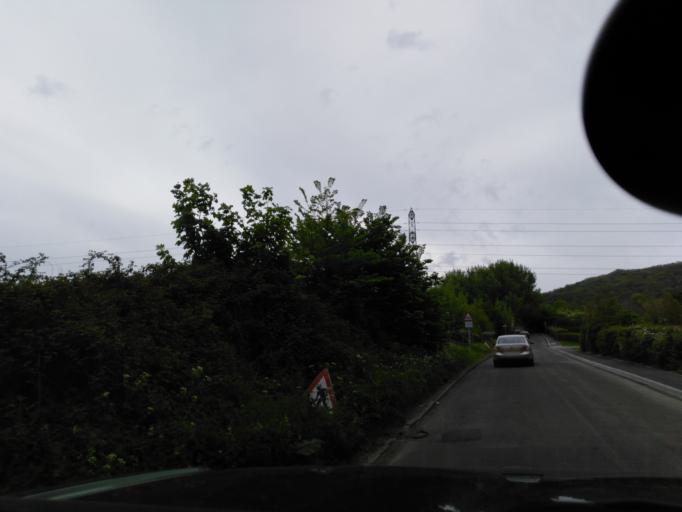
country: GB
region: England
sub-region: Bath and North East Somerset
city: Bath
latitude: 51.3999
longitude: -2.3238
